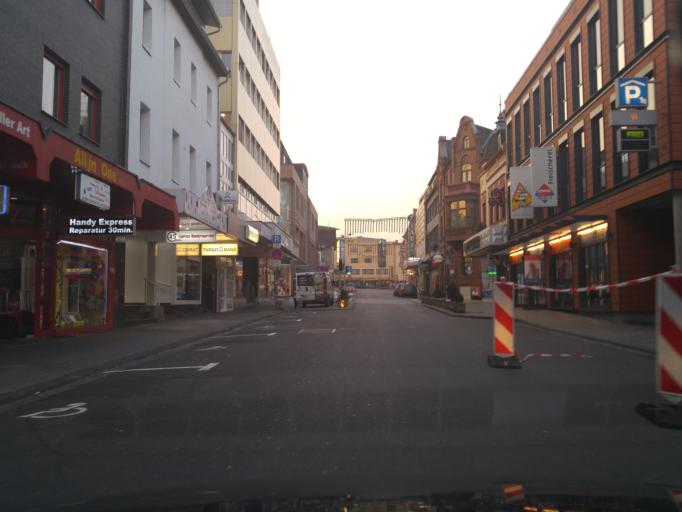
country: DE
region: Hesse
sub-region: Regierungsbezirk Giessen
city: Limburg an der Lahn
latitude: 50.3868
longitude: 8.0625
